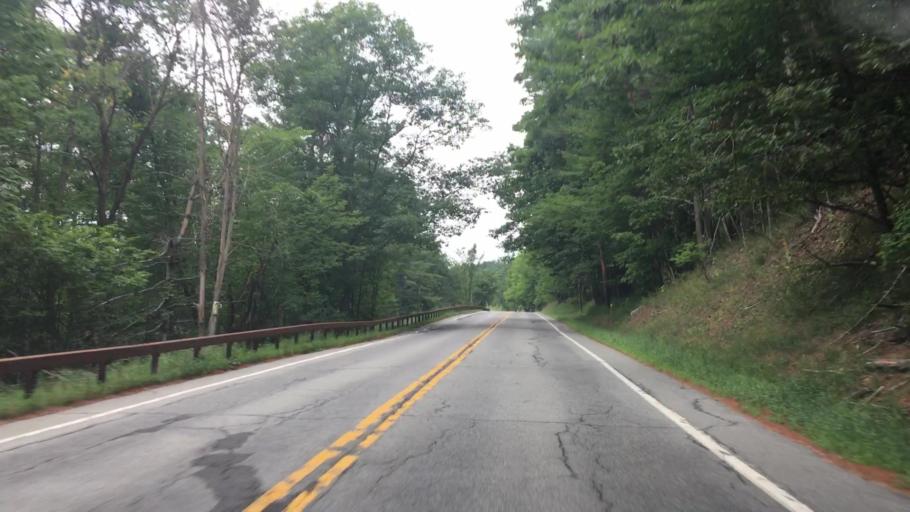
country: US
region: New York
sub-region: Essex County
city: Elizabethtown
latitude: 44.4042
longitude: -73.7042
